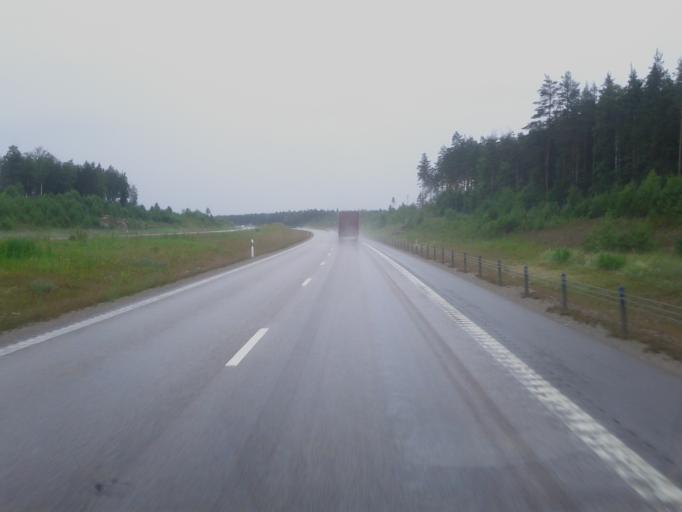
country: SE
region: Uppsala
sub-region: Tierps Kommun
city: Tierp
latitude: 60.3022
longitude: 17.5210
